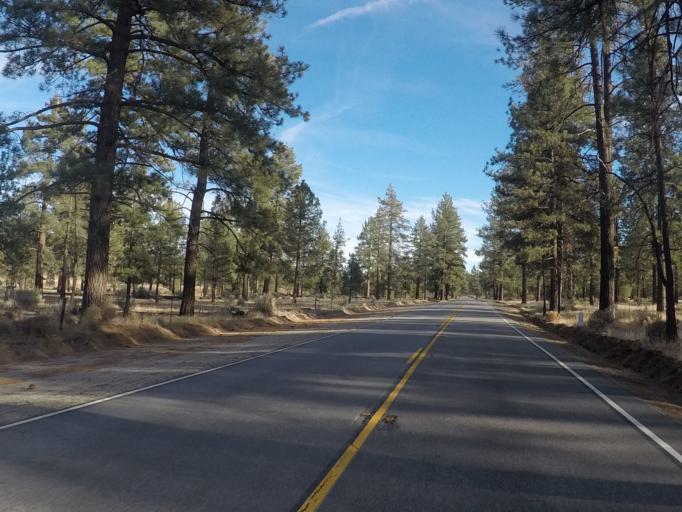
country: US
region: California
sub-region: Riverside County
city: Anza
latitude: 33.6279
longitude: -116.6381
